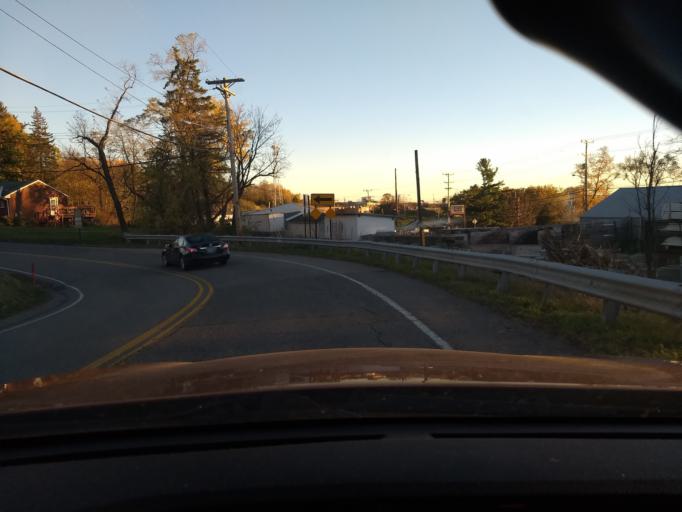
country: US
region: Pennsylvania
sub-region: Allegheny County
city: Baldwin
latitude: 40.3461
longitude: -79.9860
